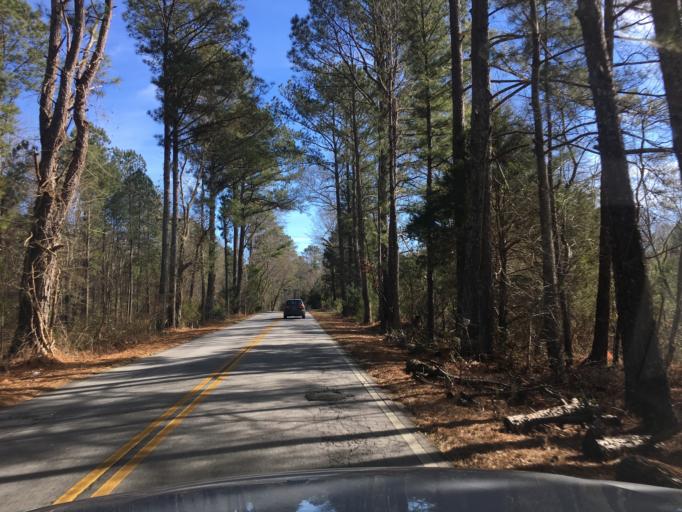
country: US
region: Georgia
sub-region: Rockdale County
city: Lakeview Estates
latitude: 33.7549
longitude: -84.0444
